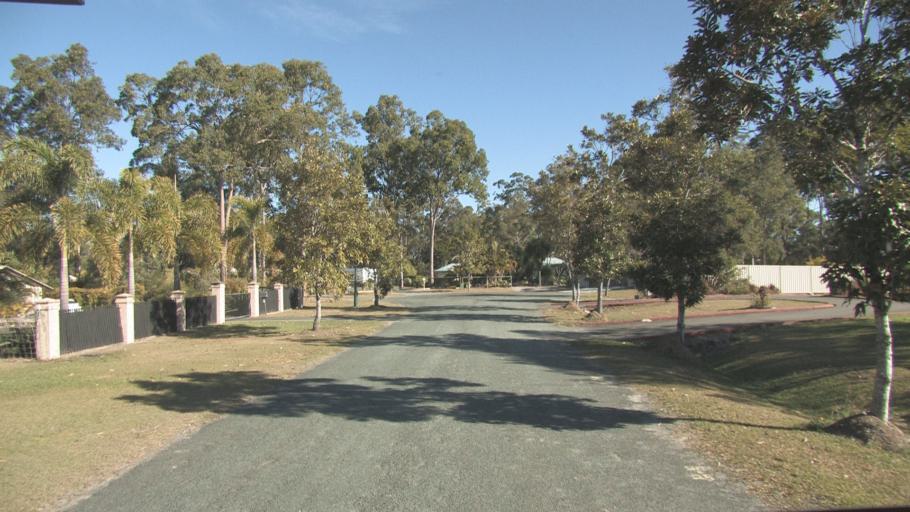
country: AU
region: Queensland
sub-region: Ipswich
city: Springfield Lakes
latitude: -27.7320
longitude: 152.9227
